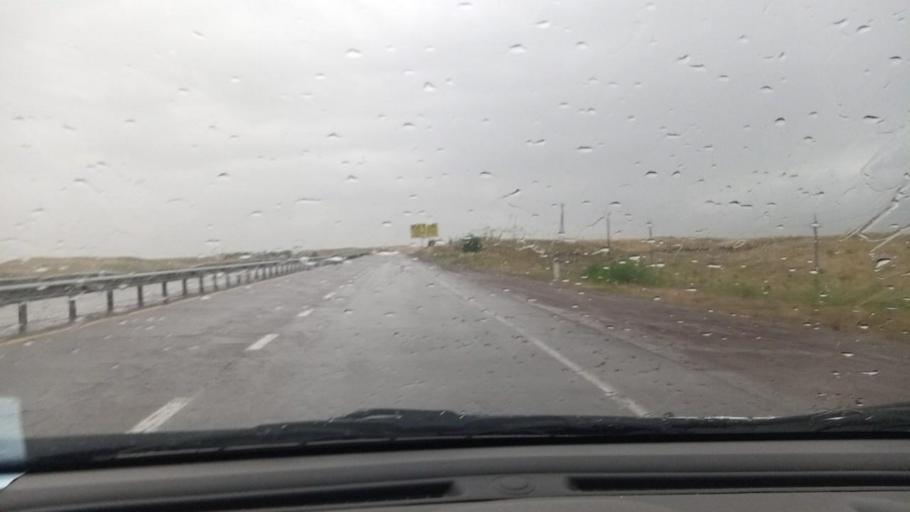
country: UZ
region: Toshkent
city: Ohangaron
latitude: 40.9716
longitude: 69.5467
